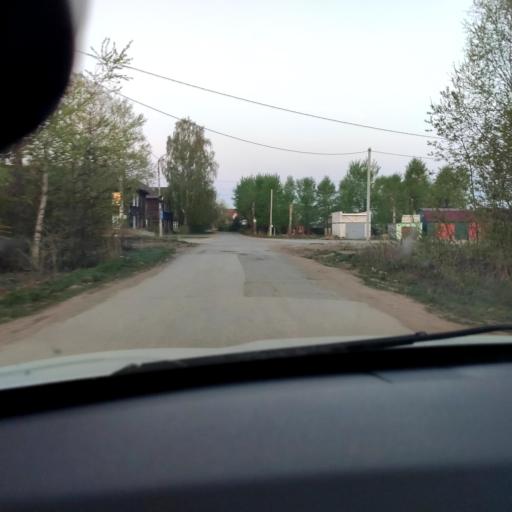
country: RU
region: Perm
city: Krasnokamsk
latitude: 58.0605
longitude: 55.8031
